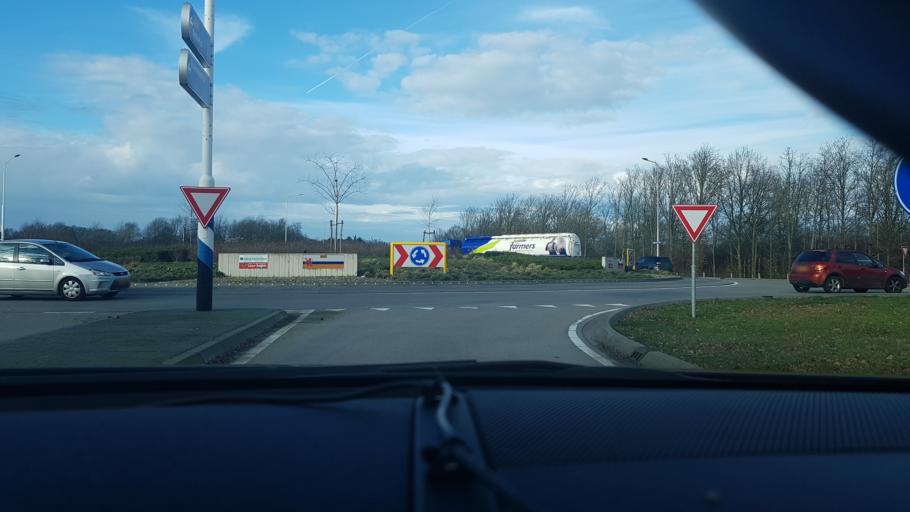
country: NL
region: Limburg
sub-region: Gemeente Peel en Maas
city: Maasbree
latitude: 51.3519
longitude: 6.0141
